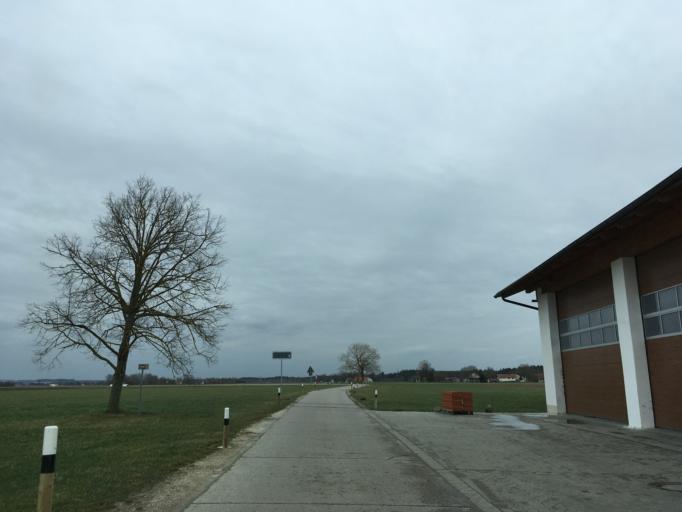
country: DE
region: Bavaria
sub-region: Upper Bavaria
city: Waldkraiburg
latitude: 48.2342
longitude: 12.3988
